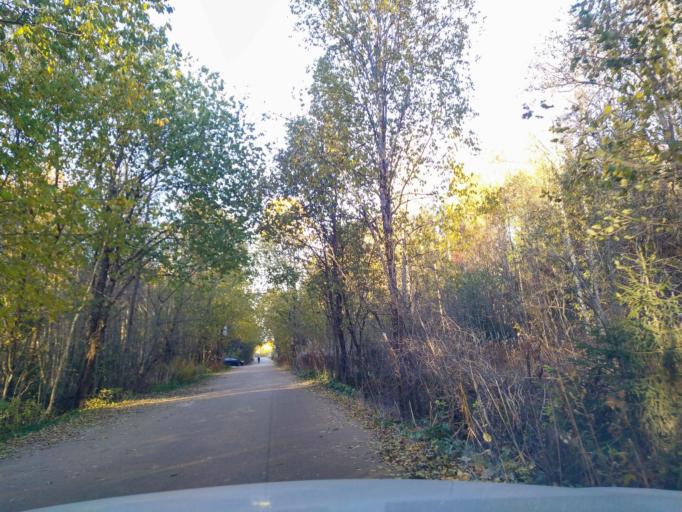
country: RU
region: Leningrad
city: Siverskiy
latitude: 59.2974
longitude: 30.0344
